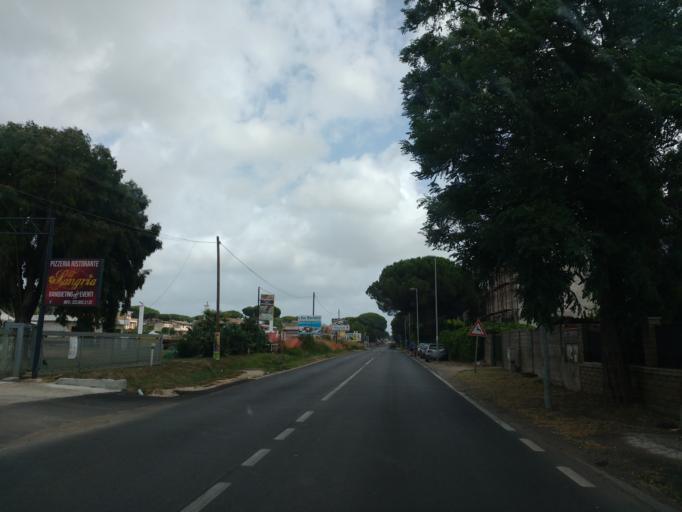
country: IT
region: Latium
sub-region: Citta metropolitana di Roma Capitale
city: Lavinio
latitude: 41.4915
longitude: 12.5956
